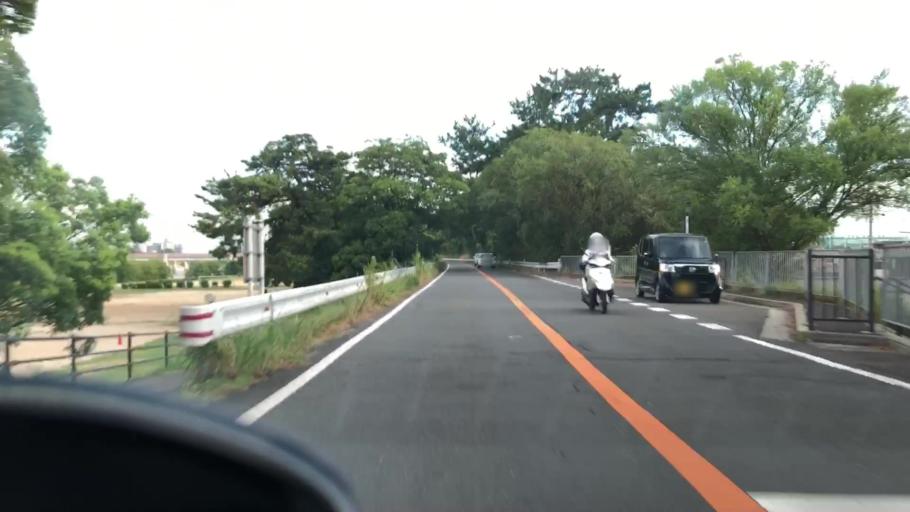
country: JP
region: Hyogo
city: Itami
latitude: 34.7534
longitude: 135.3727
